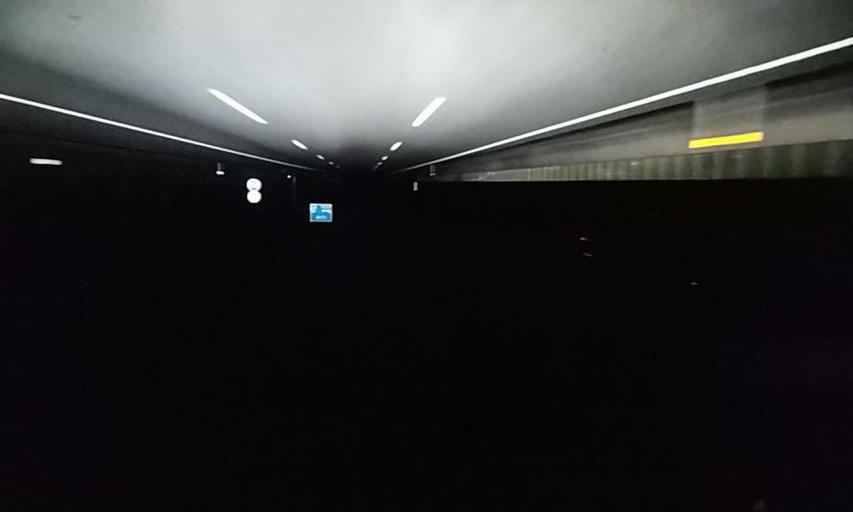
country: PT
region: Aveiro
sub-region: Estarreja
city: Beduido
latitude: 40.7852
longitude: -8.5460
